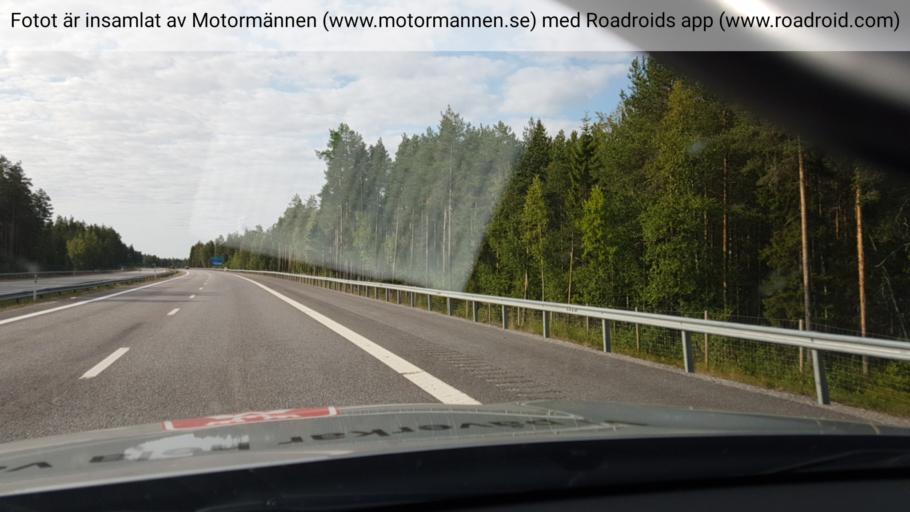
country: SE
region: Norrbotten
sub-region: Pitea Kommun
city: Pitea
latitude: 65.3432
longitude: 21.4379
